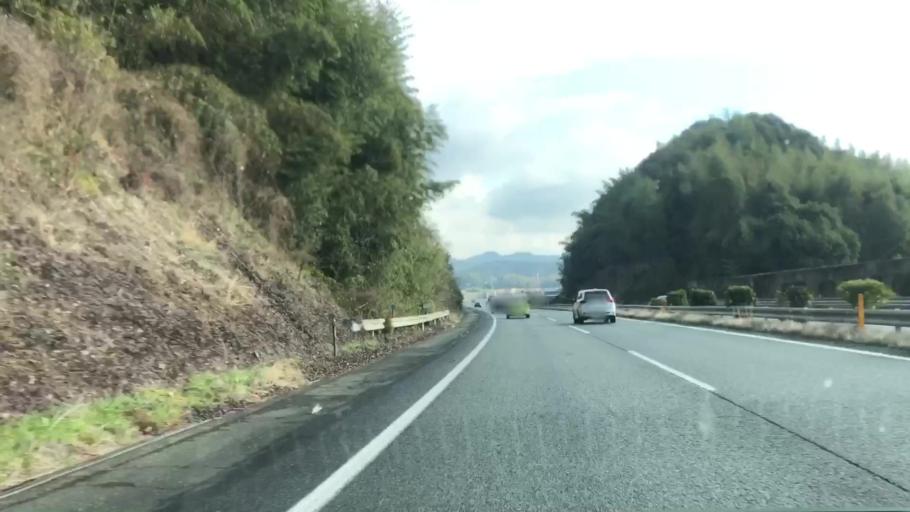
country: JP
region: Kumamoto
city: Tamana
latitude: 32.9978
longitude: 130.5935
